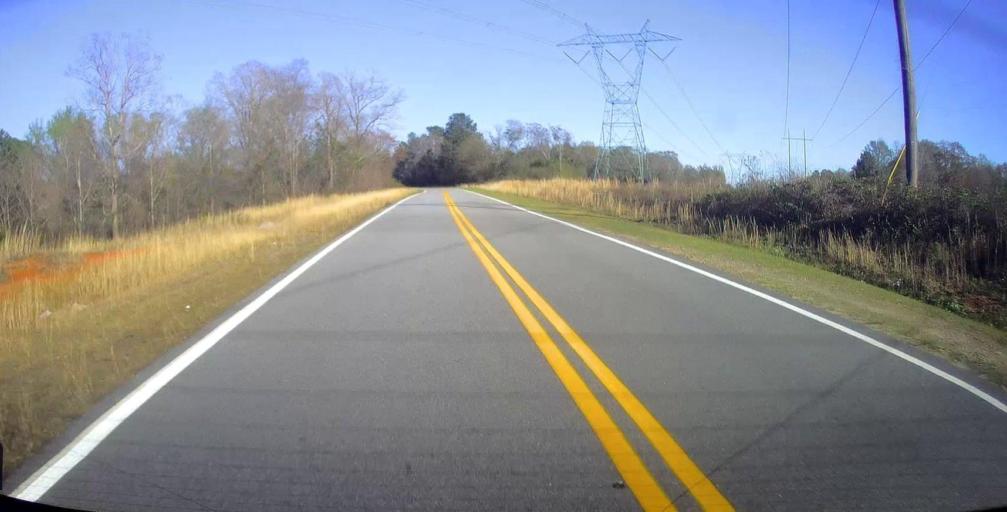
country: US
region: Georgia
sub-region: Peach County
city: Byron
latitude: 32.6733
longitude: -83.8242
